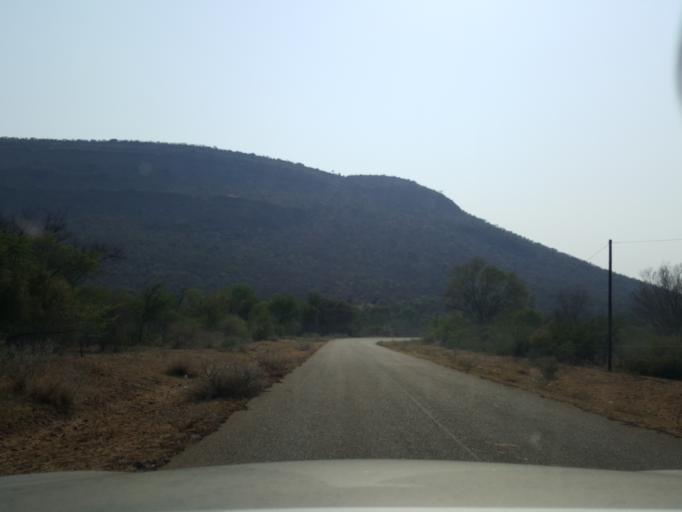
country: BW
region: South East
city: Lobatse
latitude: -25.3272
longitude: 25.7707
